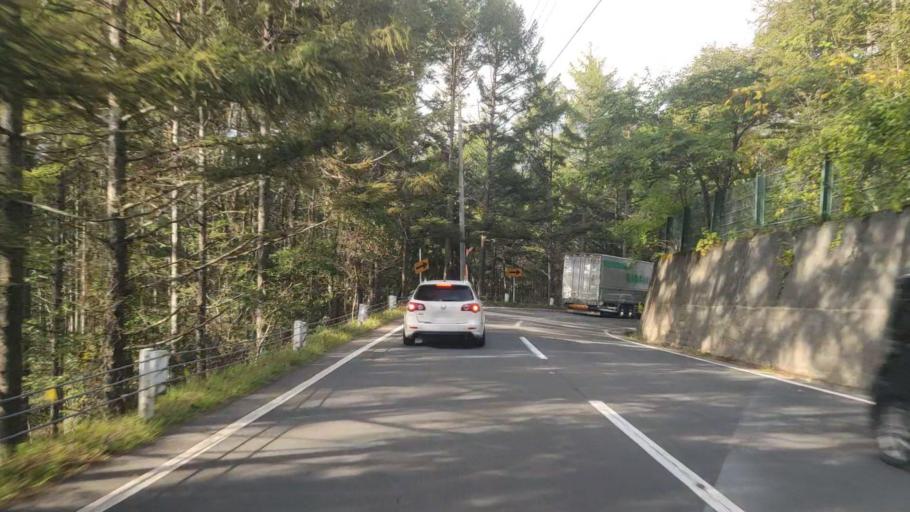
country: JP
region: Nagano
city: Ueda
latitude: 36.4915
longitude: 138.3929
